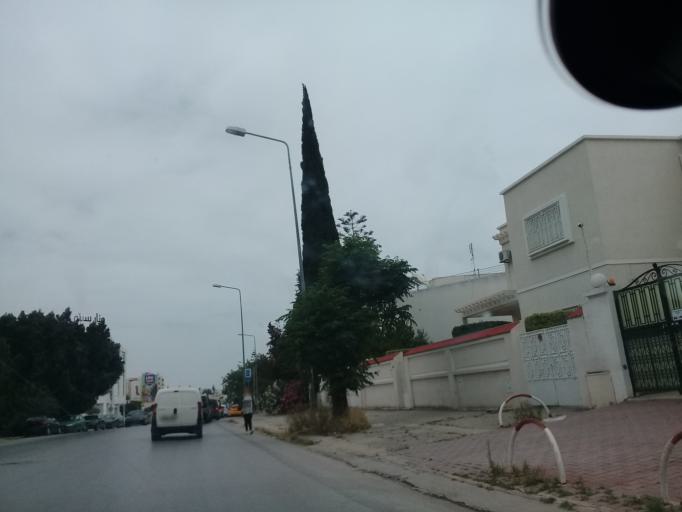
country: TN
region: Tunis
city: Tunis
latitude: 36.8410
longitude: 10.1622
